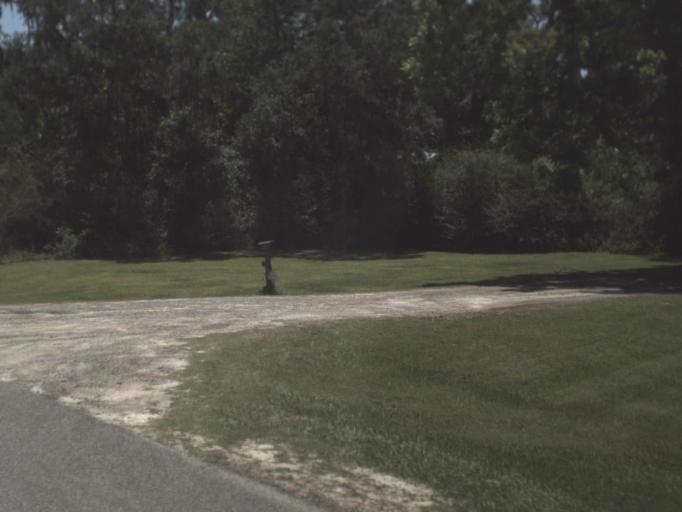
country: US
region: Florida
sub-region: Suwannee County
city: Live Oak
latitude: 30.3188
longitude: -83.0355
